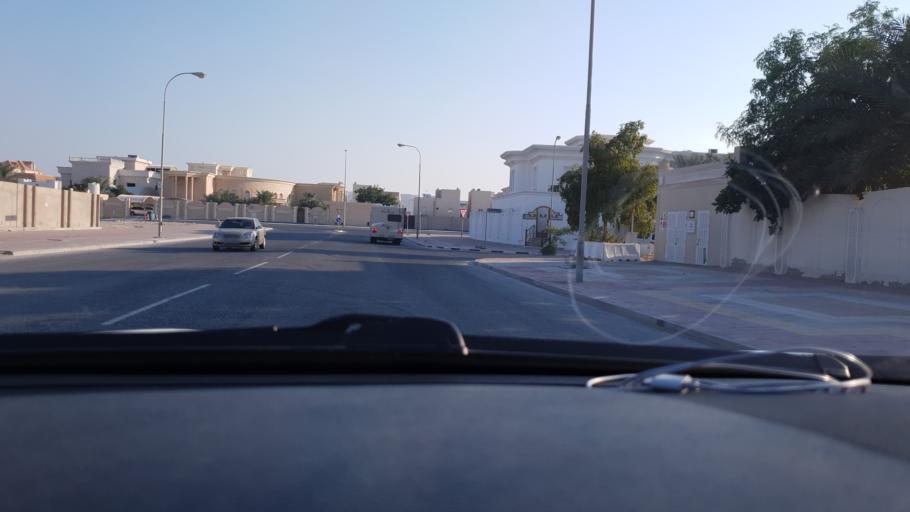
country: QA
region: Baladiyat ad Dawhah
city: Doha
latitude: 25.2343
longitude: 51.5657
